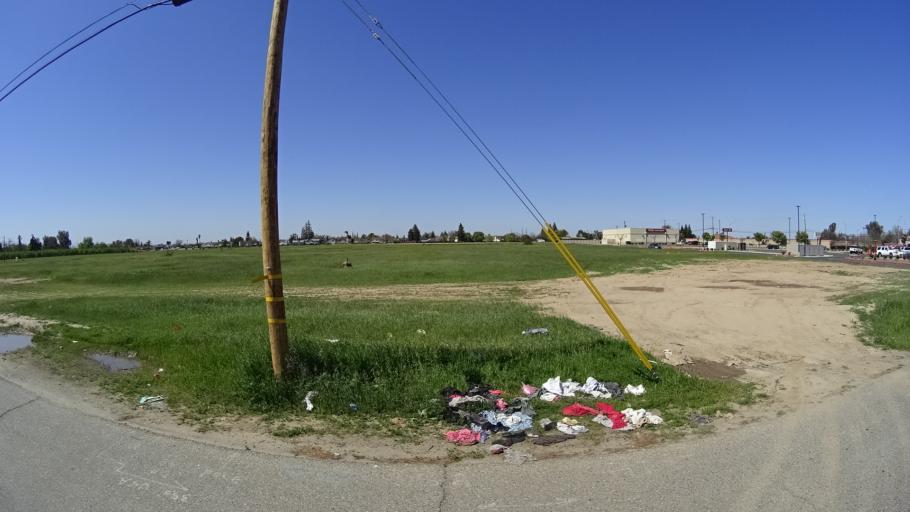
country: US
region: California
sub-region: Fresno County
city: West Park
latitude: 36.7708
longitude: -119.8443
